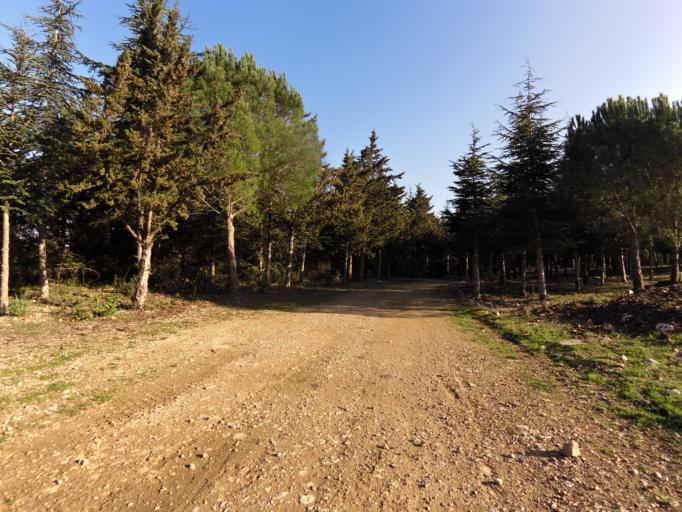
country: FR
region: Languedoc-Roussillon
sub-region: Departement de l'Herault
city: Villetelle
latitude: 43.7372
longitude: 4.1294
